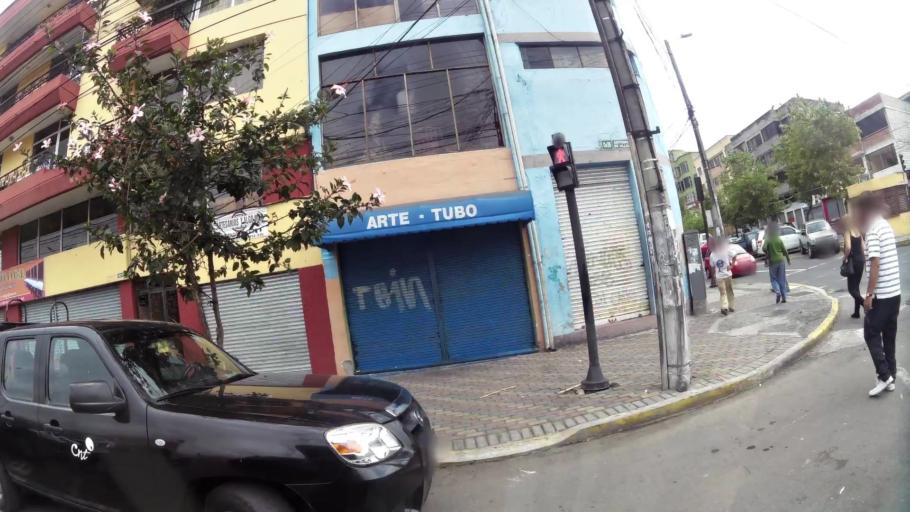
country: EC
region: Pichincha
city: Quito
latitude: -0.1993
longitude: -78.4997
